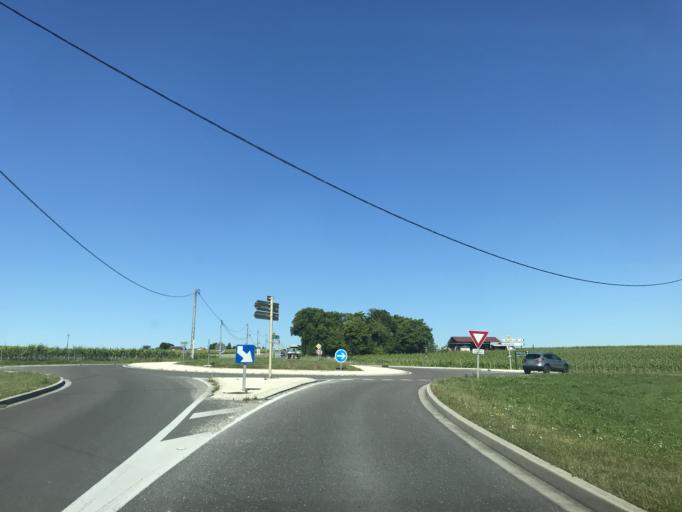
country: FR
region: Poitou-Charentes
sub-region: Departement de la Charente
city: Barbezieux-Saint-Hilaire
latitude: 45.4934
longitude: -0.2036
